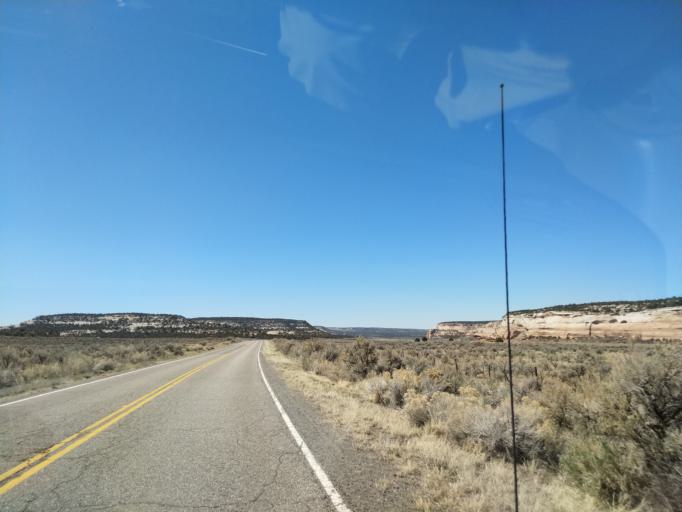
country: US
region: Colorado
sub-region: Mesa County
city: Loma
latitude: 39.0023
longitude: -108.8490
